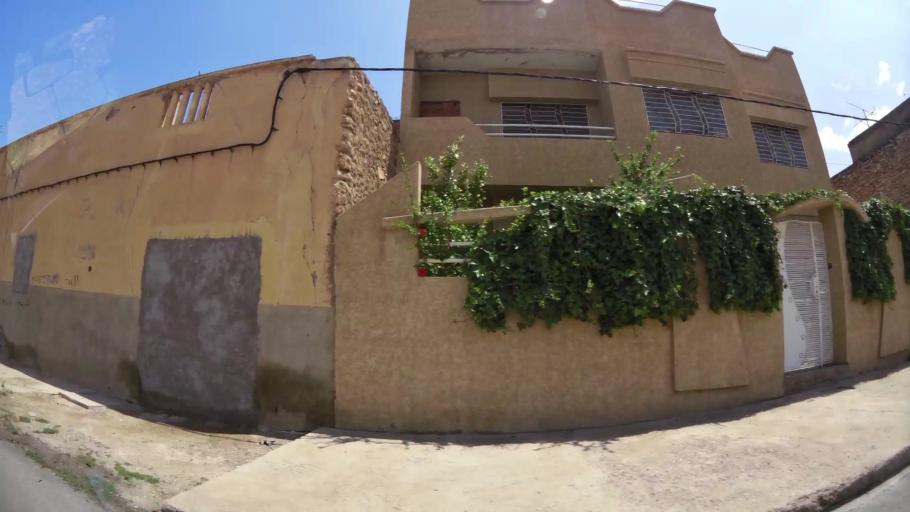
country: MA
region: Oriental
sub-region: Oujda-Angad
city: Oujda
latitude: 34.6822
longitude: -1.8882
